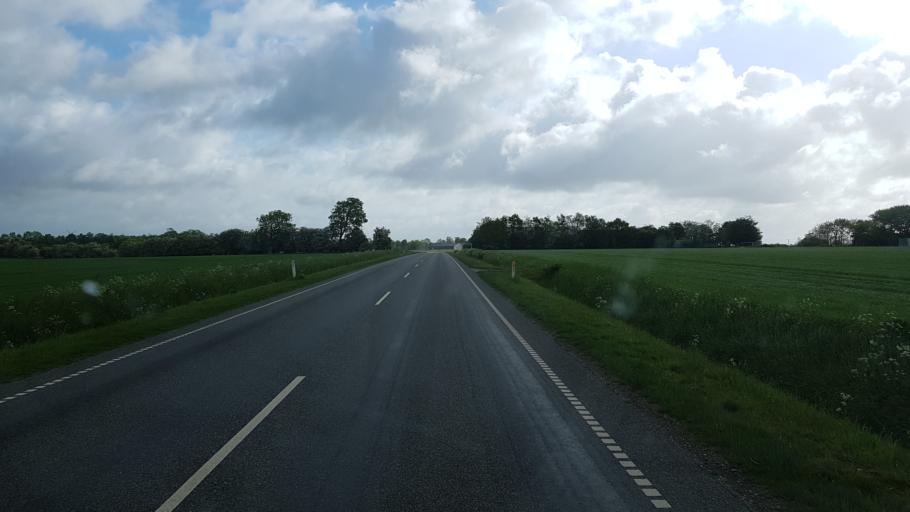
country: DK
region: South Denmark
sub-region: Vejen Kommune
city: Vejen
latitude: 55.4091
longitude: 9.1277
